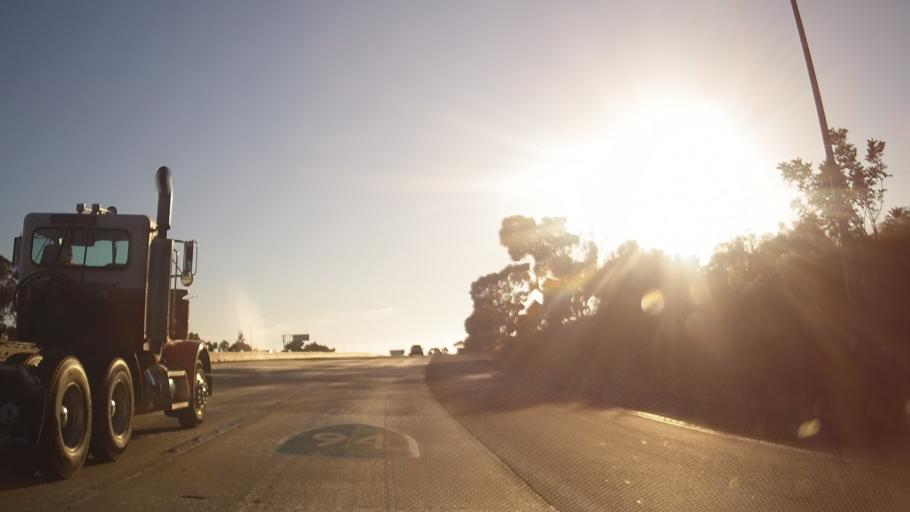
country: US
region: California
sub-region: San Diego County
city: National City
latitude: 32.7188
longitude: -117.0863
